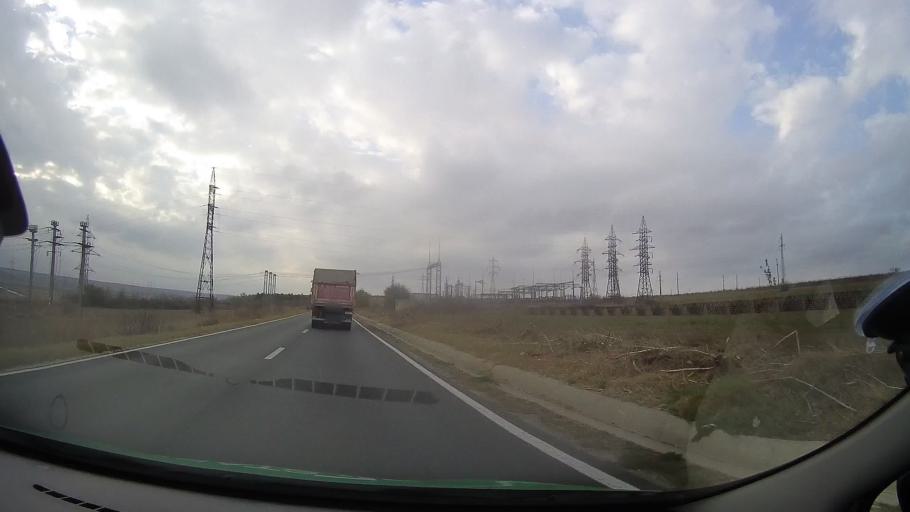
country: RO
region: Constanta
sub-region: Comuna Mircea Voda
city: Satu Nou
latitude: 44.2709
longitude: 28.2005
